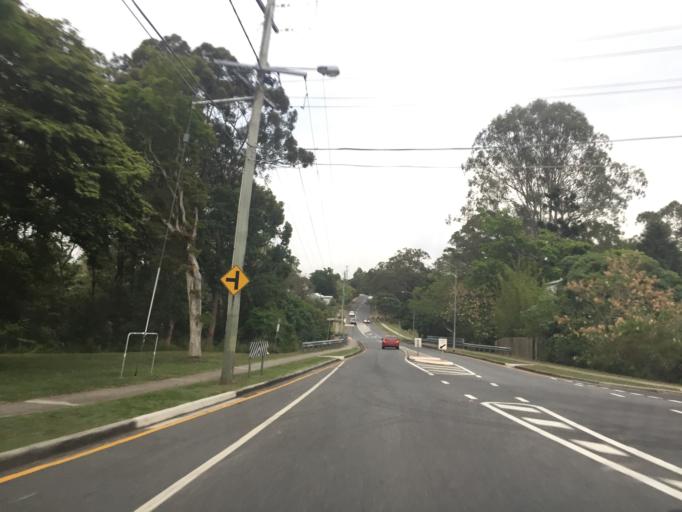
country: AU
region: Queensland
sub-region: Brisbane
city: Milton
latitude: -27.4525
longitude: 152.9799
